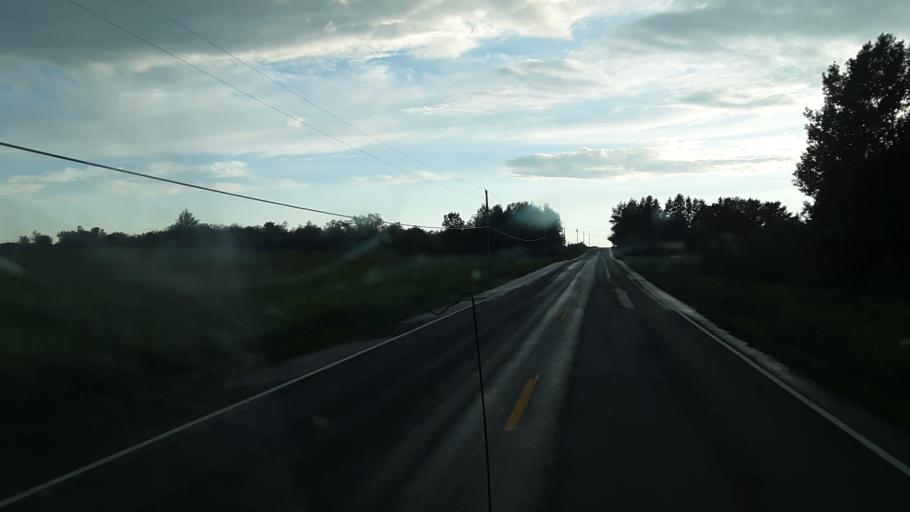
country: US
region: Maine
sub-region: Aroostook County
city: Easton
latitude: 46.6756
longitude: -67.9510
